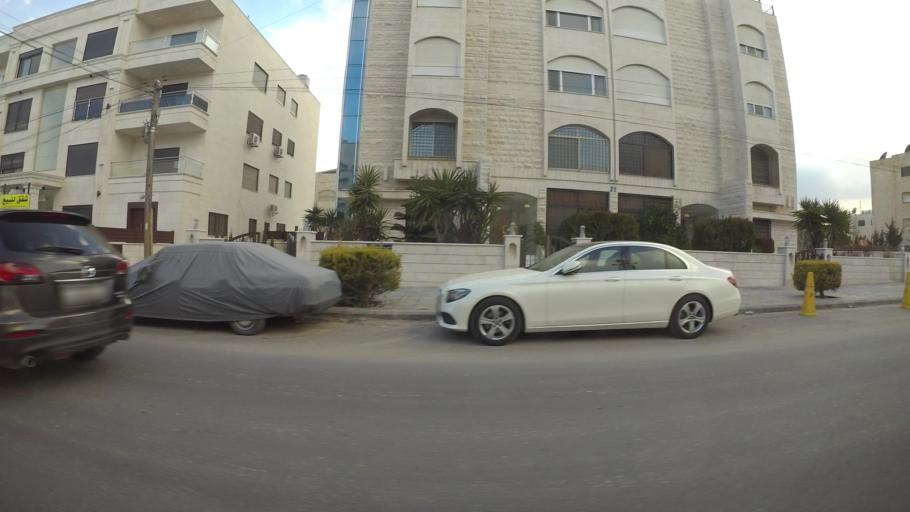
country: JO
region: Amman
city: Al Jubayhah
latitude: 31.9795
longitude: 35.8585
